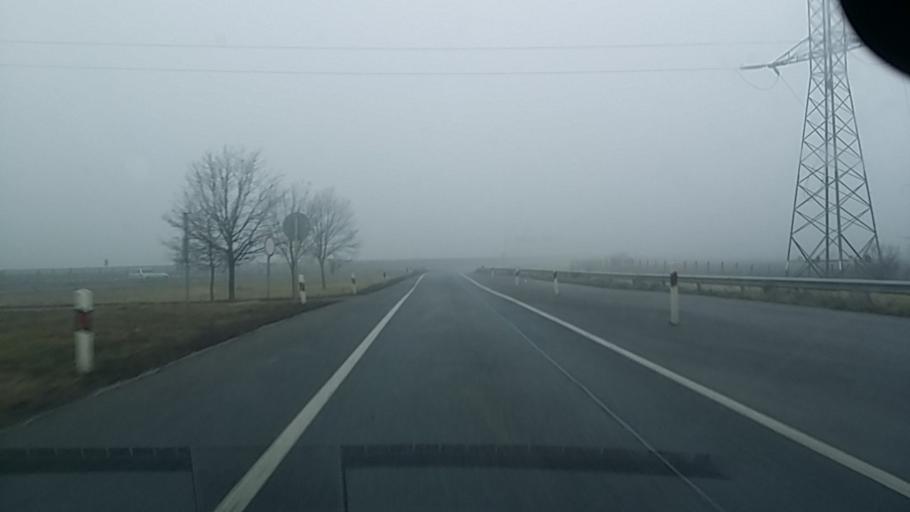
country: HU
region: Gyor-Moson-Sopron
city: Mosonmagyarovar
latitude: 47.8540
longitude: 17.2467
